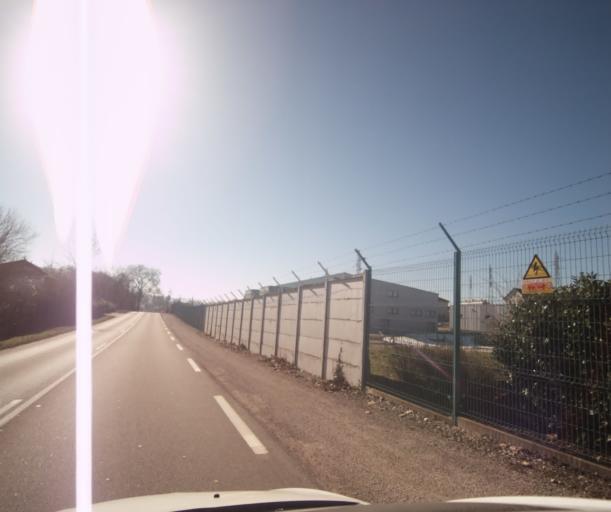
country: FR
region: Franche-Comte
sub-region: Departement du Doubs
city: Thise
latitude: 47.2677
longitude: 6.0550
